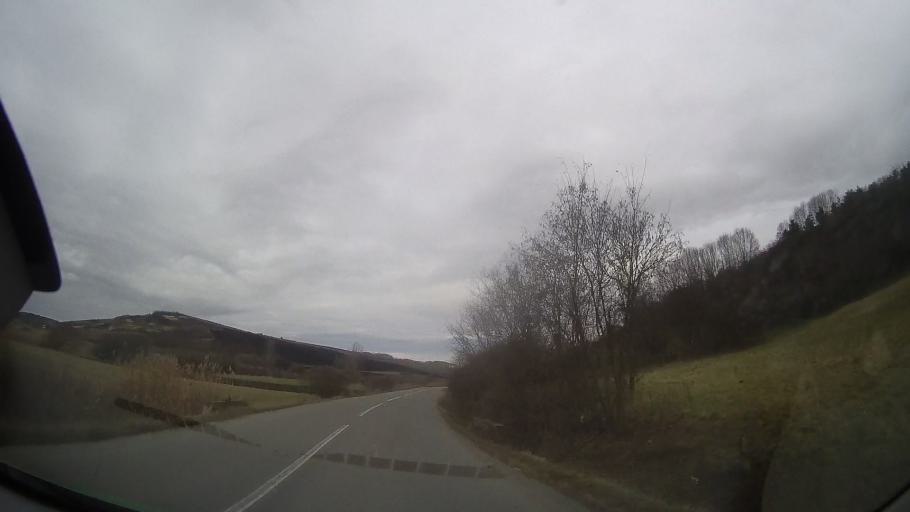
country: RO
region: Mures
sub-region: Comuna Bala
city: Bala
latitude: 46.7260
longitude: 24.5440
